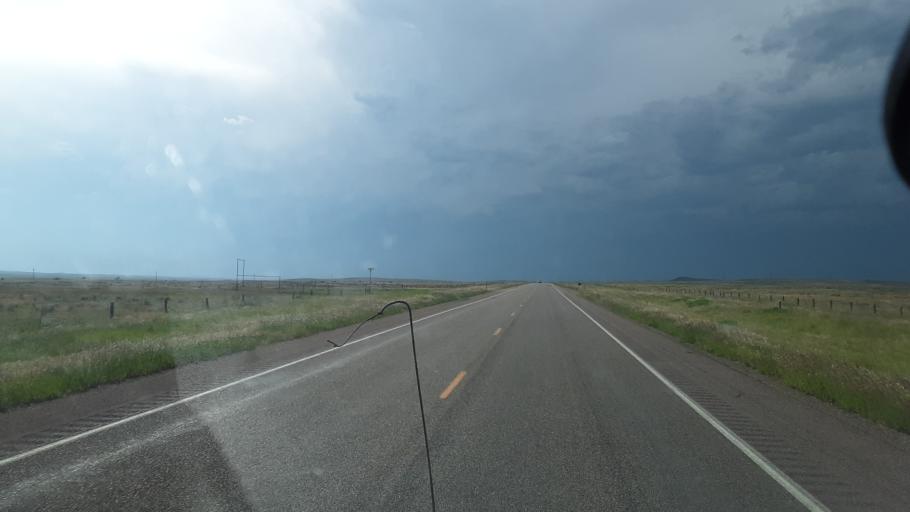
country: US
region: Montana
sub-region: Carter County
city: Ekalaka
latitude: 45.1344
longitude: -104.6801
